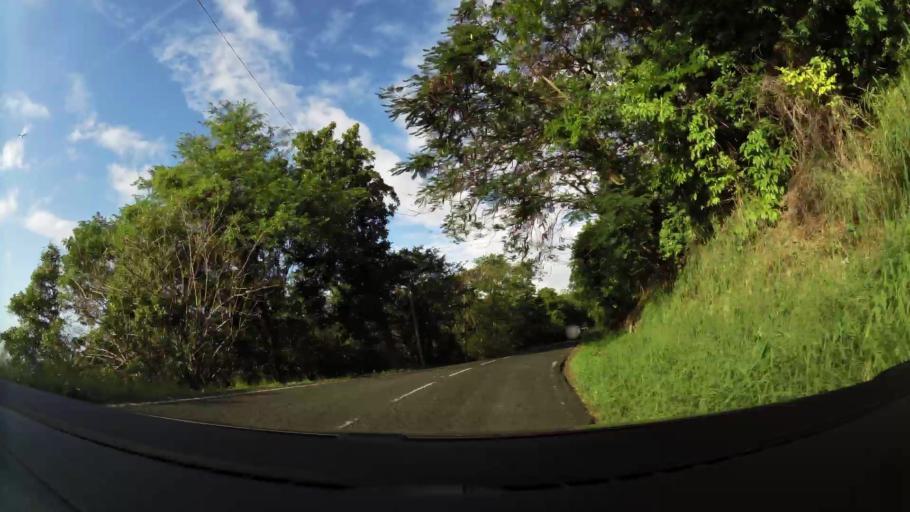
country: GP
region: Guadeloupe
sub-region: Guadeloupe
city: Bouillante
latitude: 16.1796
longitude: -61.7815
